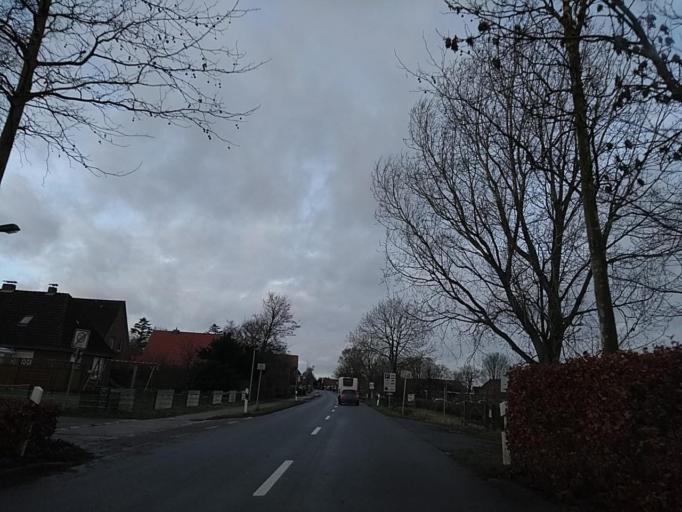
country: DE
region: Lower Saxony
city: Emden
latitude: 53.3134
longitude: 7.2868
